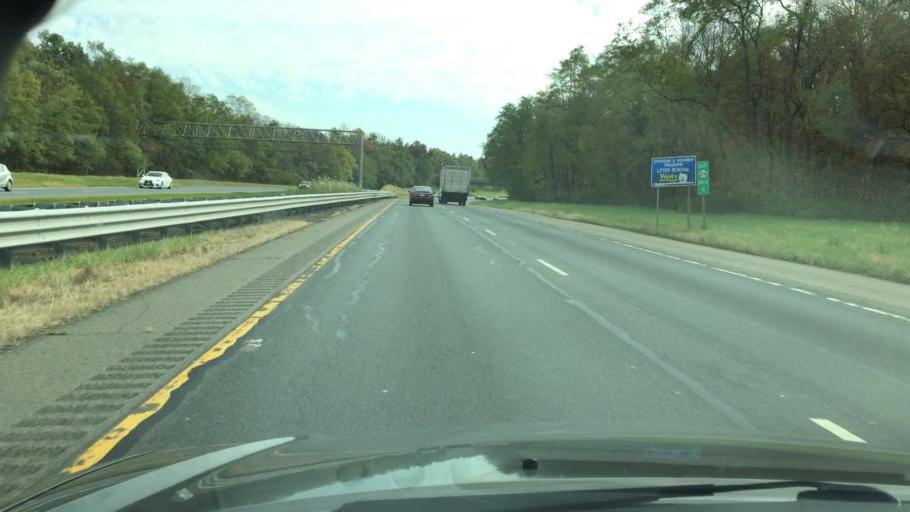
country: US
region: New Jersey
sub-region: Morris County
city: Chatham
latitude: 40.7526
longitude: -74.3775
